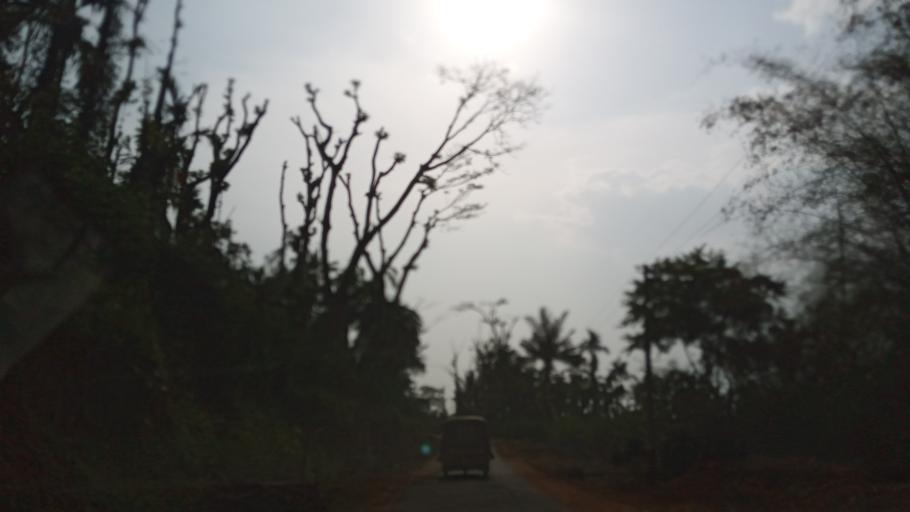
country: IN
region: Karnataka
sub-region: Chikmagalur
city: Mudigere
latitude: 13.0598
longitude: 75.6694
